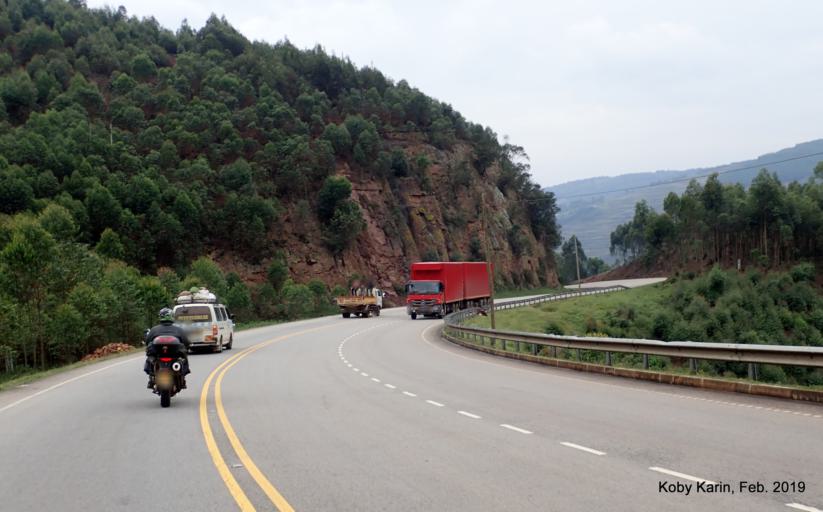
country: UG
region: Western Region
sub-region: Kabale District
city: Kabale
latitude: -1.2459
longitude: 30.0336
